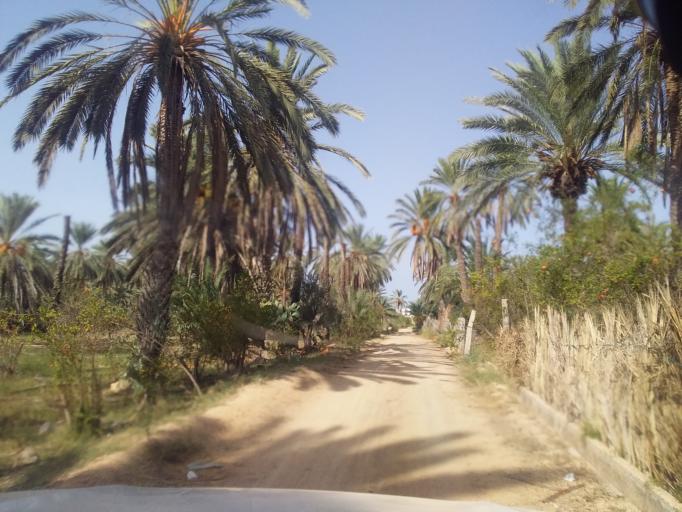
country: TN
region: Qabis
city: Gabes
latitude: 33.6278
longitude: 10.2856
